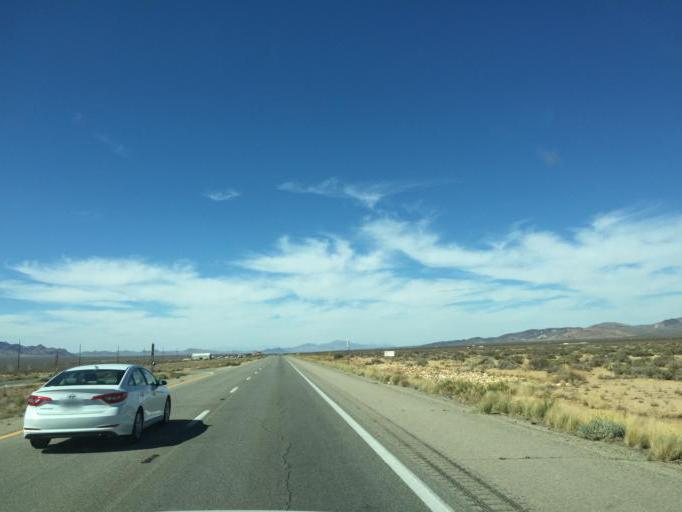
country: US
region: Arizona
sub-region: Mohave County
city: Dolan Springs
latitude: 35.5475
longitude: -114.3646
